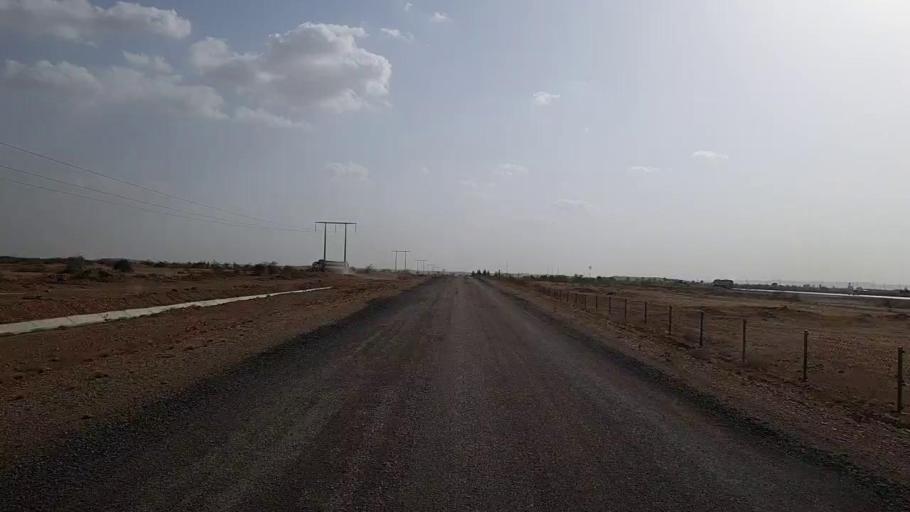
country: PK
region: Sindh
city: Kotri
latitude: 25.2674
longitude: 67.9985
